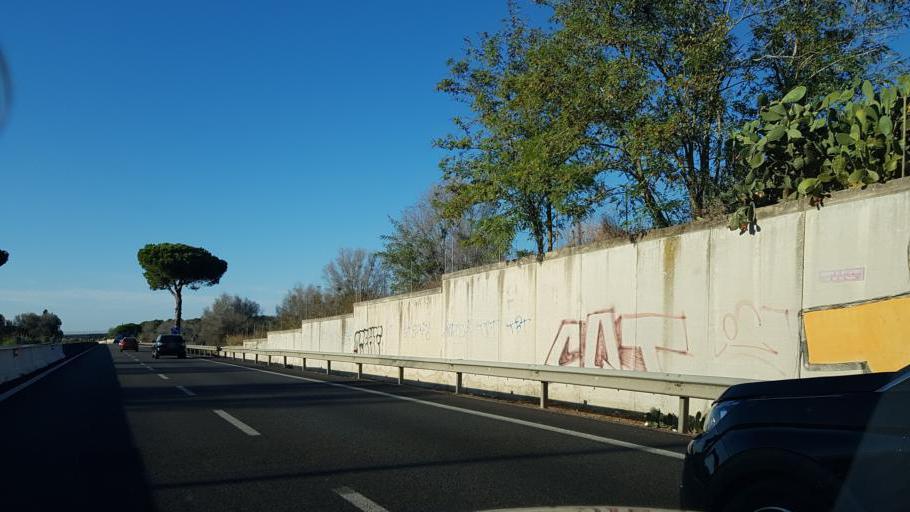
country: IT
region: Apulia
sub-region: Provincia di Brindisi
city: Torchiarolo
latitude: 40.4580
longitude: 18.0618
